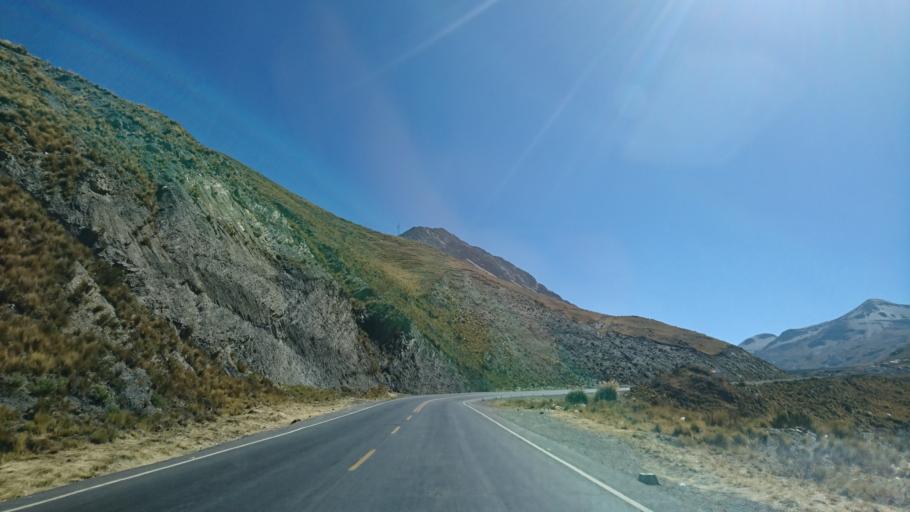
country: BO
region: La Paz
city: La Paz
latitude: -16.4181
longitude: -68.0550
